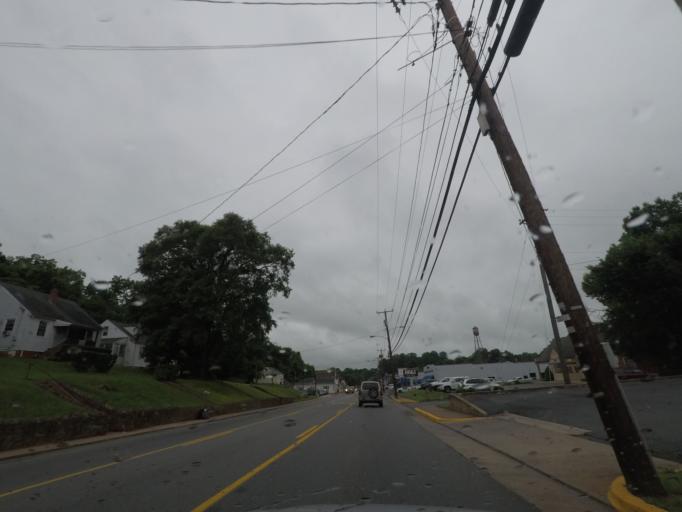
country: US
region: Virginia
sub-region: Orange County
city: Orange
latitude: 38.2490
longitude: -78.1128
